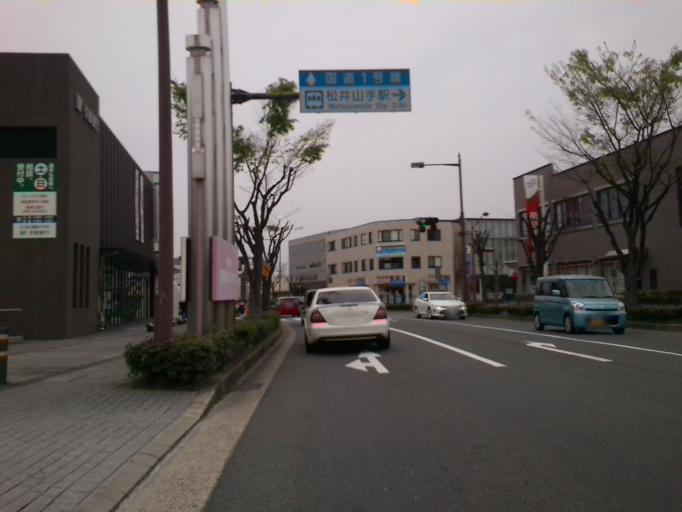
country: JP
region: Kyoto
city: Tanabe
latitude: 34.8321
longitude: 135.7286
